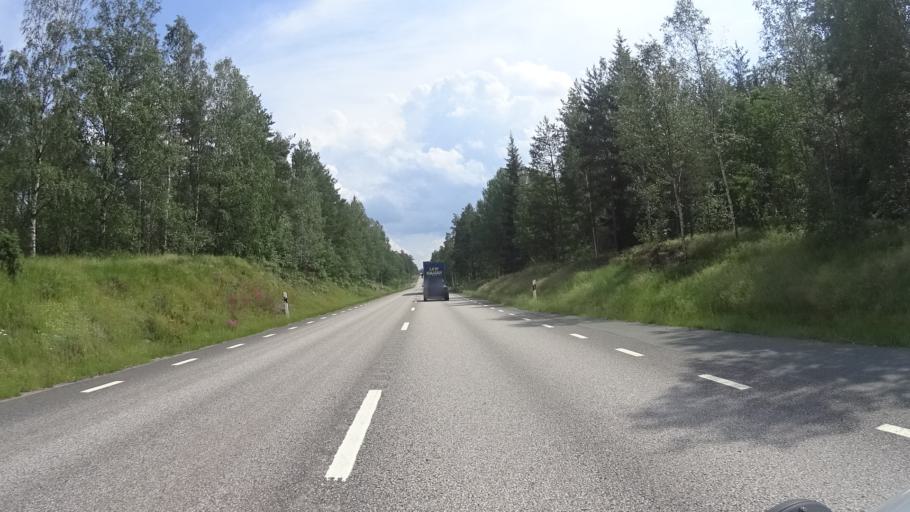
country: SE
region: Kalmar
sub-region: Hultsfreds Kommun
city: Hultsfred
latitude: 57.4851
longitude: 15.8298
